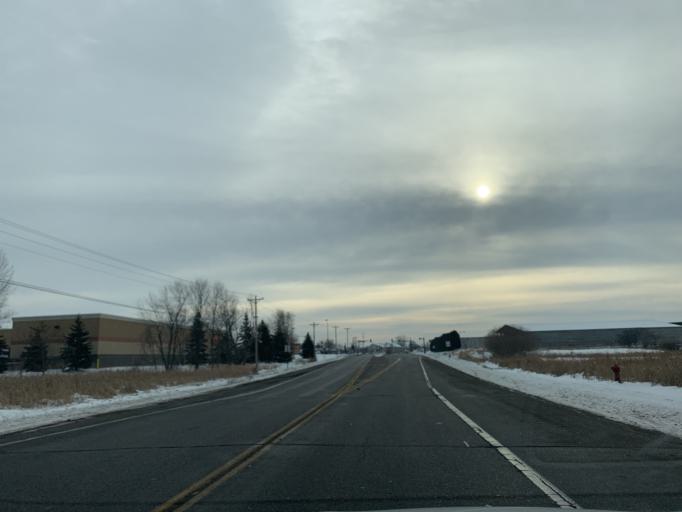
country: US
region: Minnesota
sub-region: Washington County
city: Forest Lake
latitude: 45.2834
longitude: -93.0129
